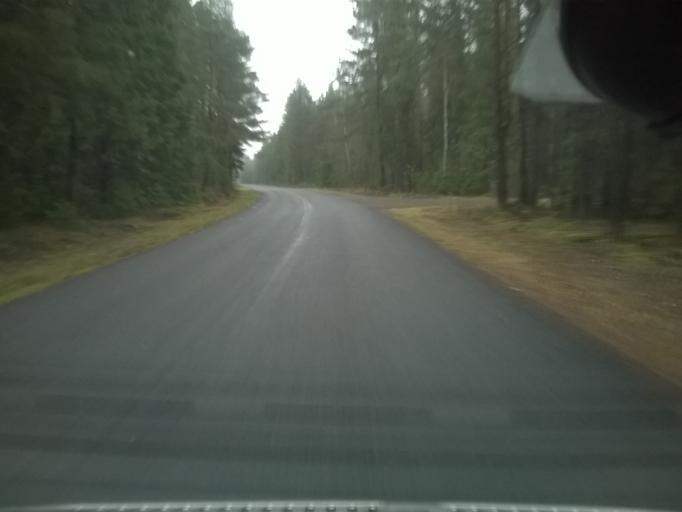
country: EE
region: Harju
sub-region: Nissi vald
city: Riisipere
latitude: 59.1222
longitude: 24.4024
